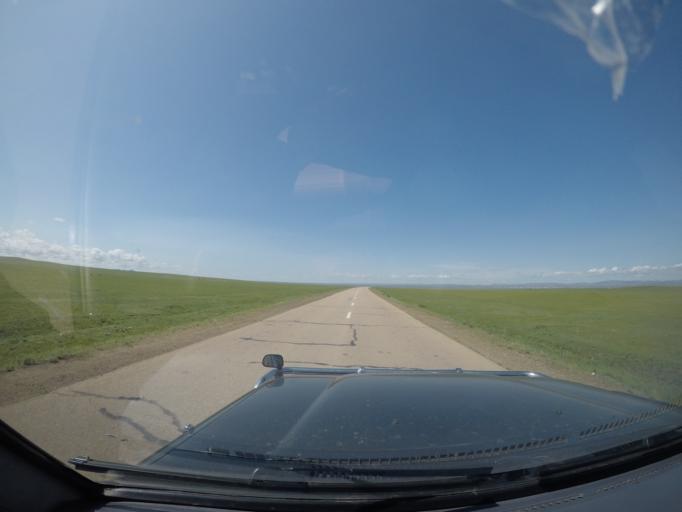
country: MN
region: Hentiy
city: Bayan
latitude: 47.2781
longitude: 110.7919
